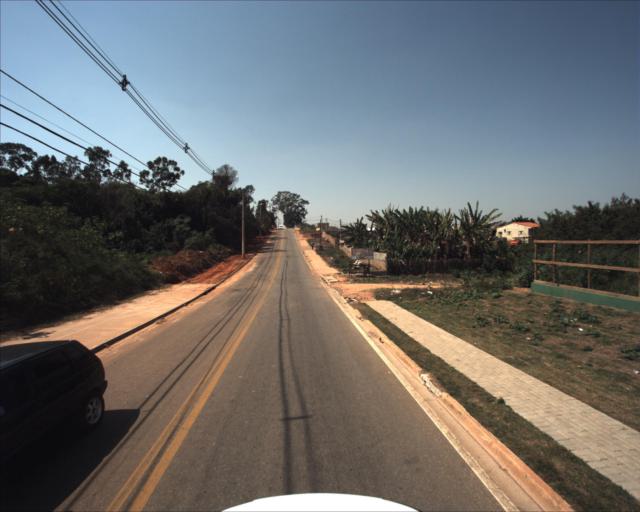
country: BR
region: Sao Paulo
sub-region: Sorocaba
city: Sorocaba
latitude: -23.4552
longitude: -47.4990
